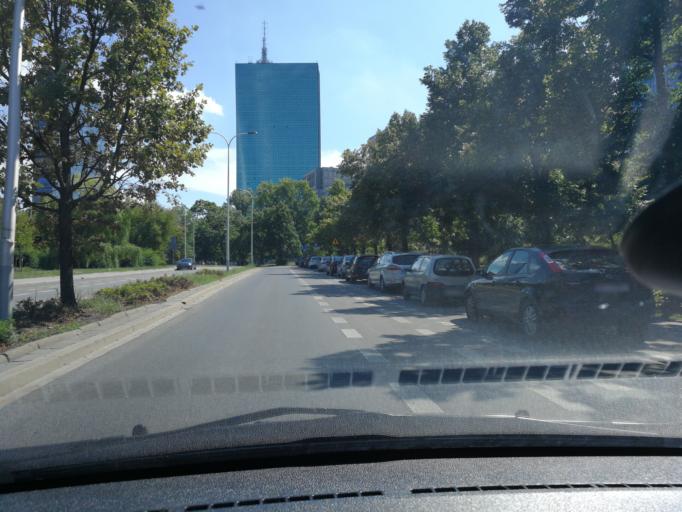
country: PL
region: Masovian Voivodeship
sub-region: Warszawa
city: Zoliborz
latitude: 52.2573
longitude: 20.9956
